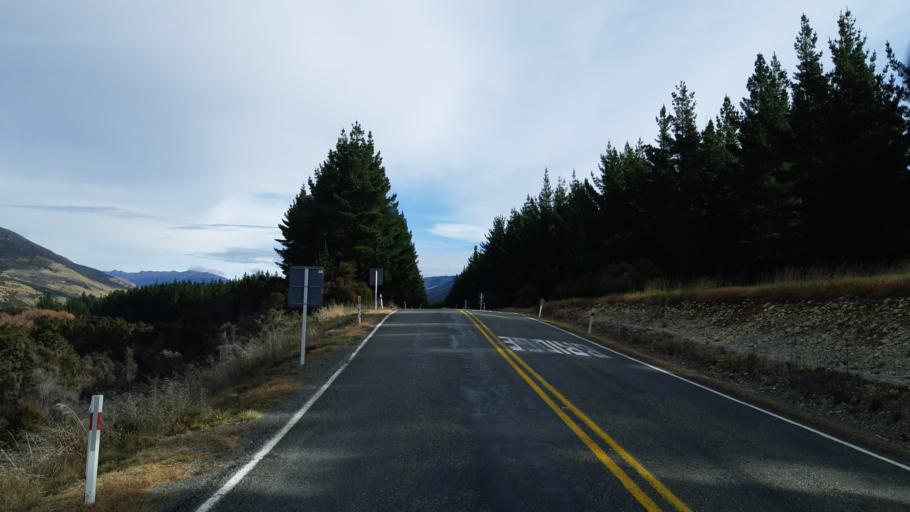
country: NZ
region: Tasman
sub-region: Tasman District
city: Wakefield
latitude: -41.7164
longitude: 173.0794
